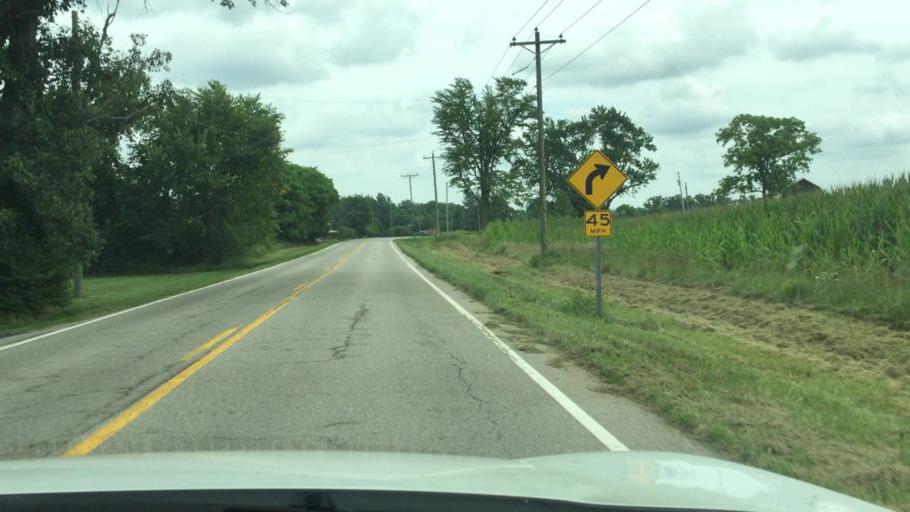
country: US
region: Ohio
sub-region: Champaign County
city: North Lewisburg
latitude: 40.2343
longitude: -83.4663
